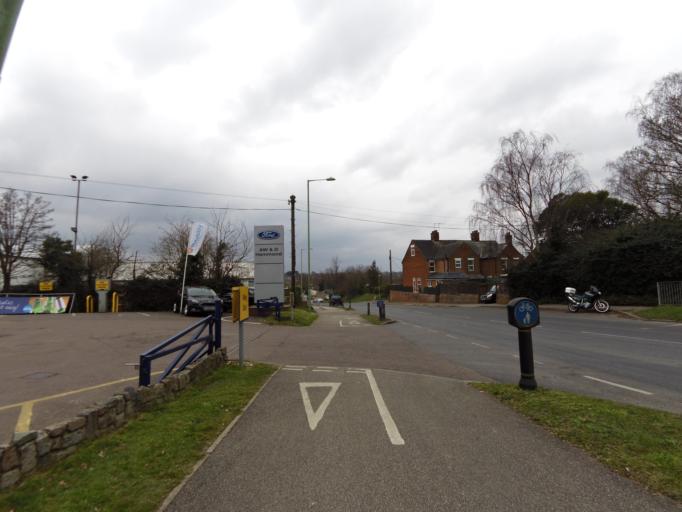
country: GB
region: England
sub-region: Suffolk
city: Halesworth
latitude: 52.3471
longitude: 1.5035
